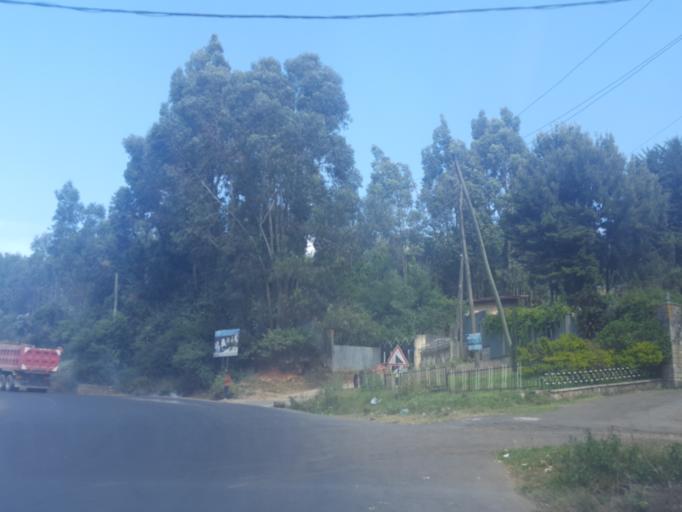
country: ET
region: Adis Abeba
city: Addis Ababa
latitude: 9.0738
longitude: 38.7382
